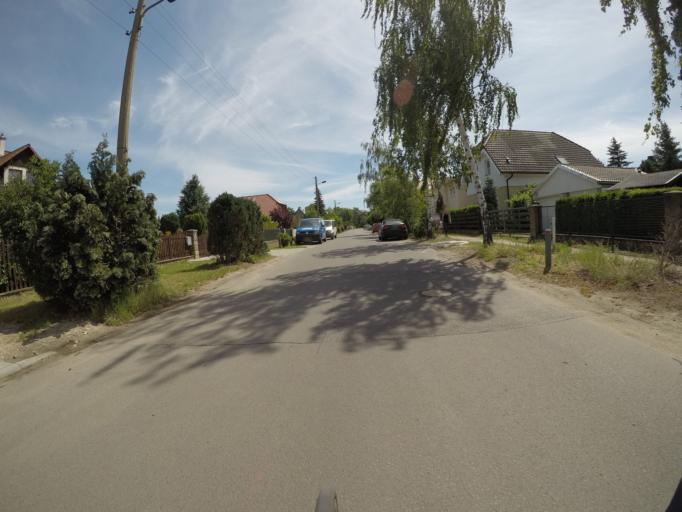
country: DE
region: Berlin
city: Mahlsdorf
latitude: 52.4943
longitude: 13.6115
